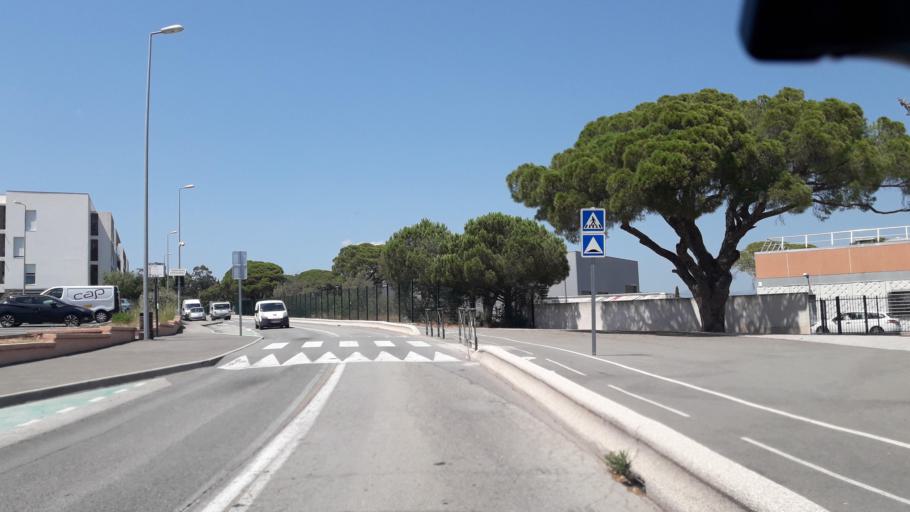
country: FR
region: Provence-Alpes-Cote d'Azur
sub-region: Departement du Var
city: Frejus
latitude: 43.4452
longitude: 6.7555
